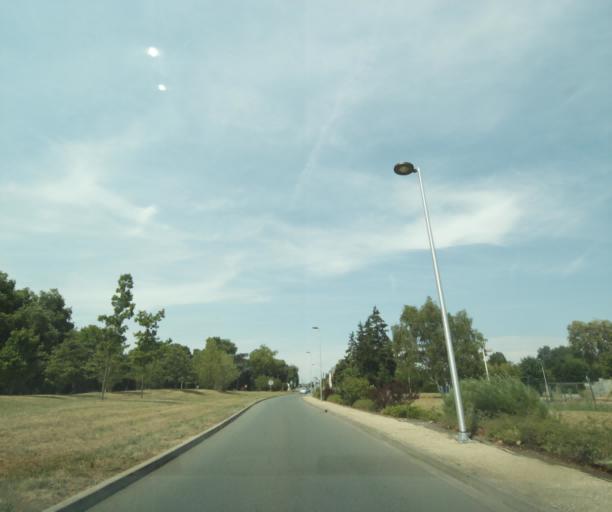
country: FR
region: Poitou-Charentes
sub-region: Departement de la Vienne
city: Antran
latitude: 46.8809
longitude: 0.5674
